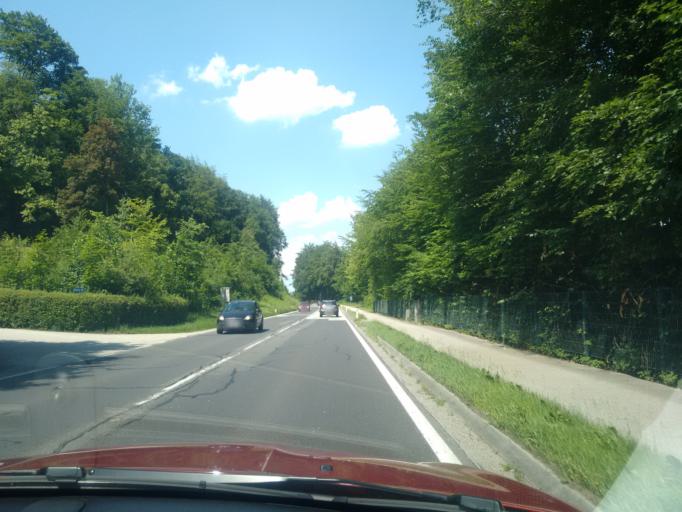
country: AT
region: Upper Austria
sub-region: Politischer Bezirk Gmunden
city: Altmunster
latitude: 47.8684
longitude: 13.7781
